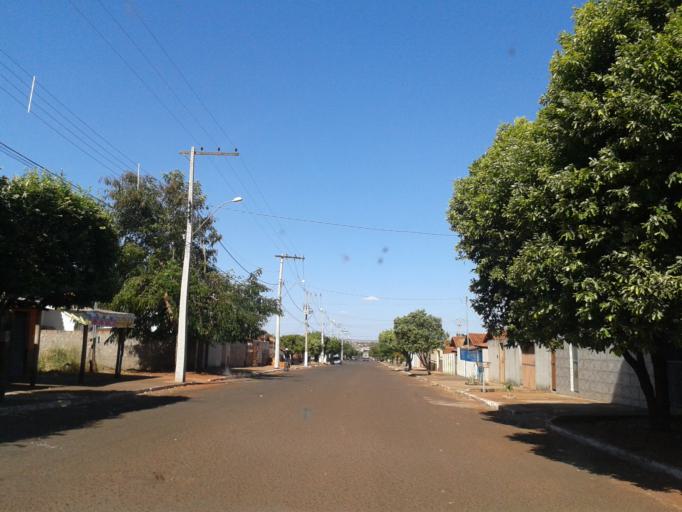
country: BR
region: Minas Gerais
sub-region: Santa Vitoria
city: Santa Vitoria
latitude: -18.8316
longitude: -50.1404
